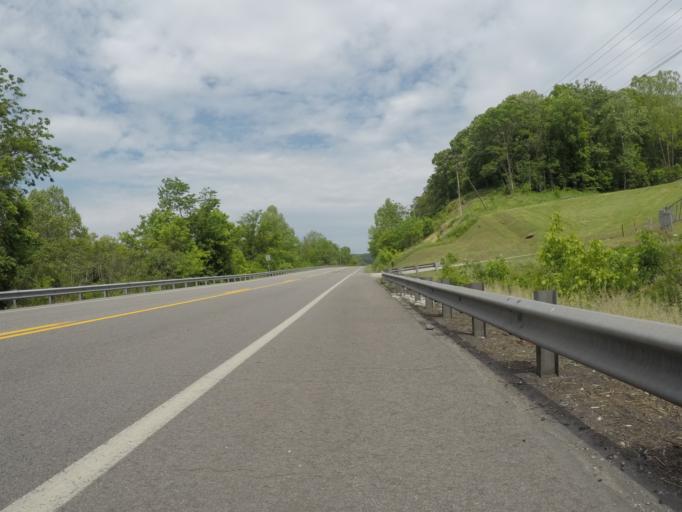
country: US
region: West Virginia
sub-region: Wayne County
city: Kenova
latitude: 38.3408
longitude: -82.5871
